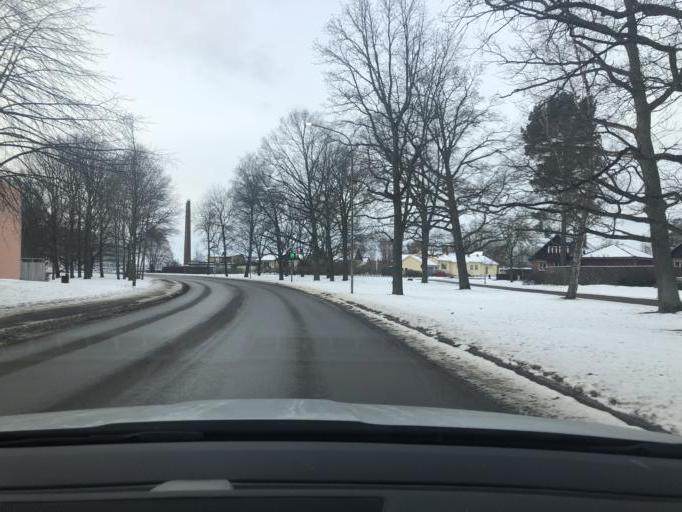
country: SE
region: OEstergoetland
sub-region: Motala Kommun
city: Motala
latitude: 58.5479
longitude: 15.0302
